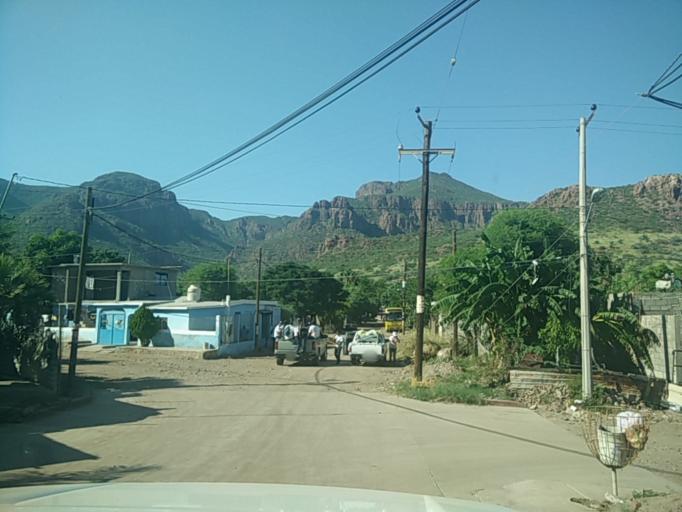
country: MX
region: Sonora
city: Heroica Guaymas
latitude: 27.9379
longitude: -110.8843
